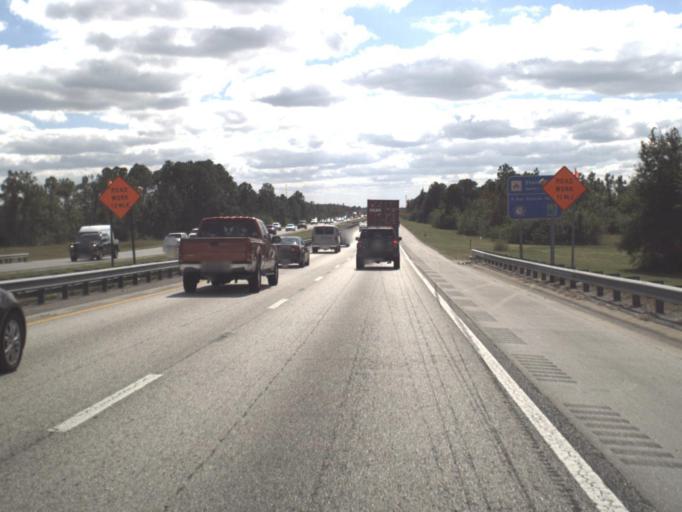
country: US
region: Florida
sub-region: Orange County
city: Southchase
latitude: 28.4036
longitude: -81.3916
